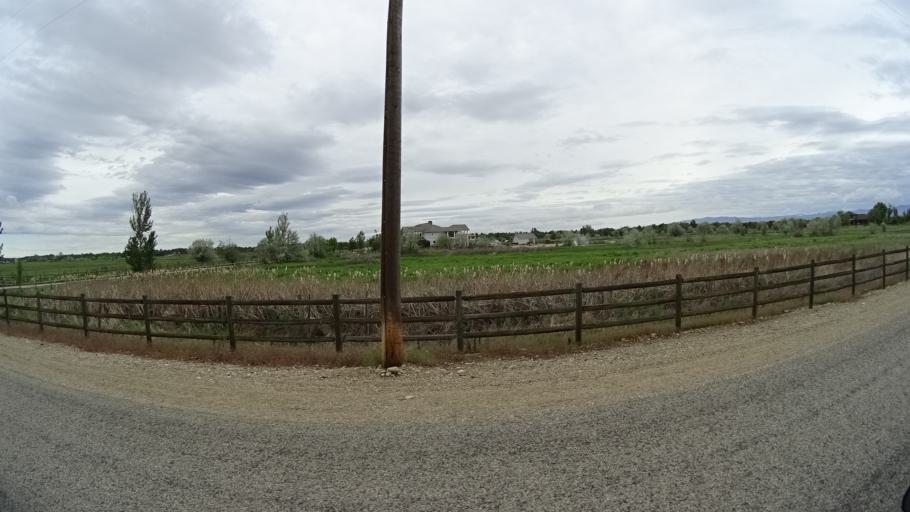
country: US
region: Idaho
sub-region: Ada County
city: Star
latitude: 43.6703
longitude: -116.4786
